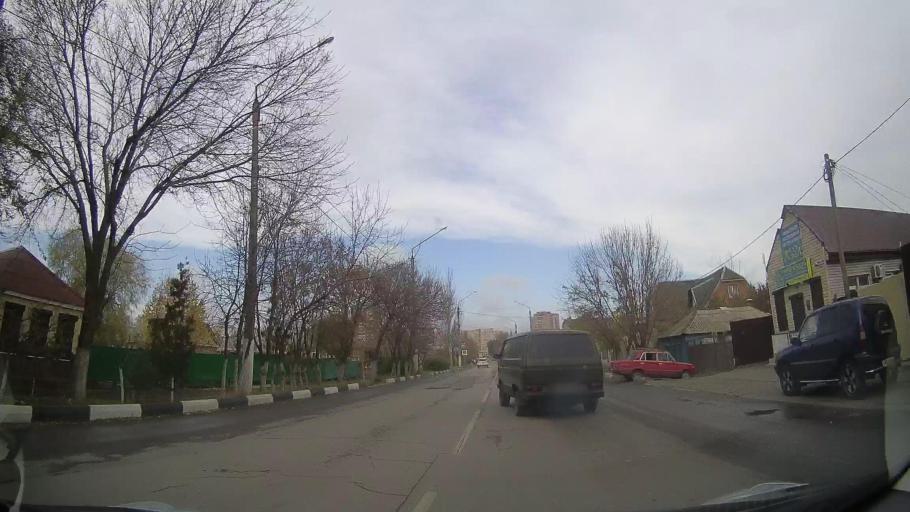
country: RU
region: Rostov
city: Bataysk
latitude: 47.1517
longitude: 39.7474
